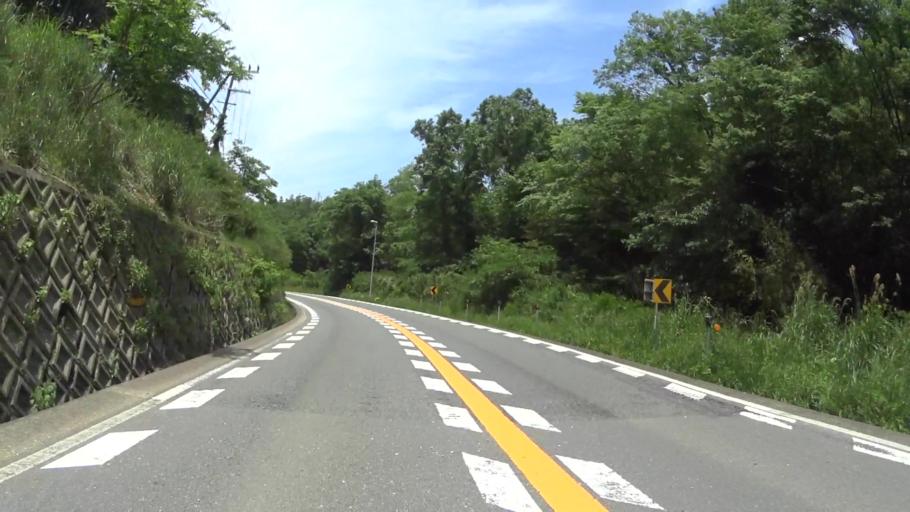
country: JP
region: Kyoto
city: Ayabe
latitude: 35.1985
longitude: 135.2831
